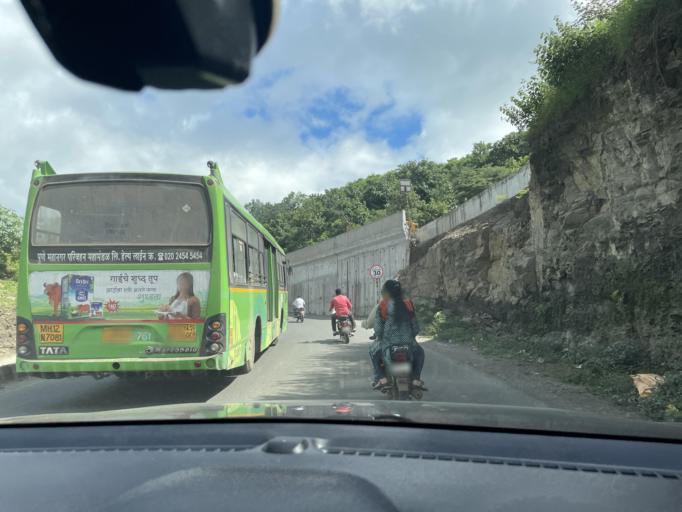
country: IN
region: Maharashtra
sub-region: Pune Division
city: Kharakvasla
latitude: 18.5057
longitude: 73.7853
